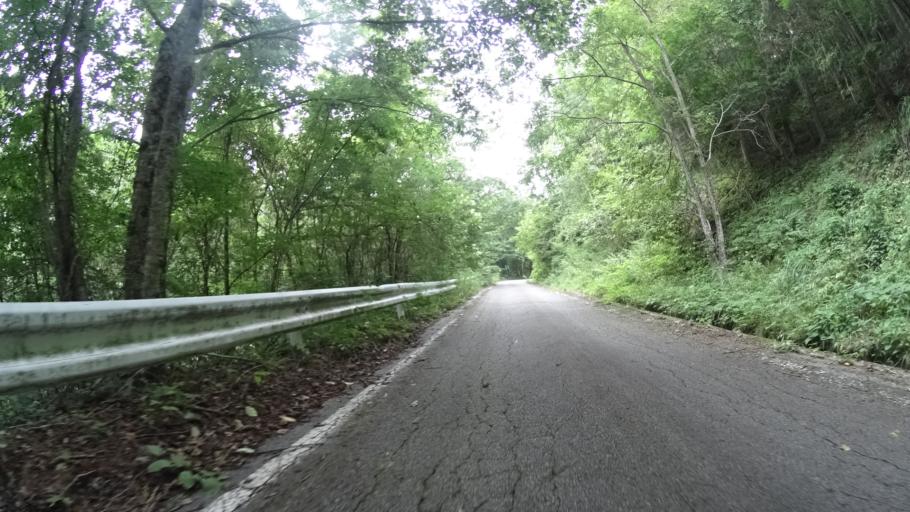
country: JP
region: Yamanashi
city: Kofu-shi
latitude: 35.8093
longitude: 138.6152
